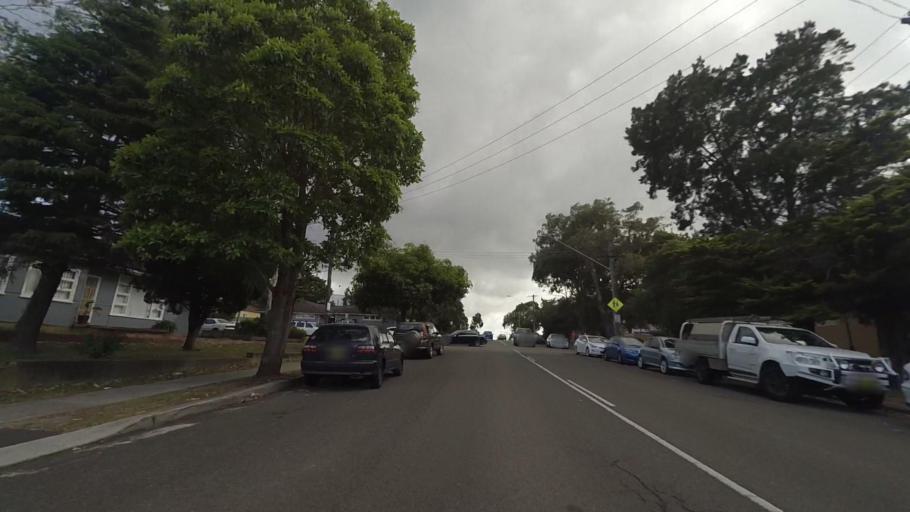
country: AU
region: New South Wales
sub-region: Sutherland Shire
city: Engadine
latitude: -34.0676
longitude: 151.0109
